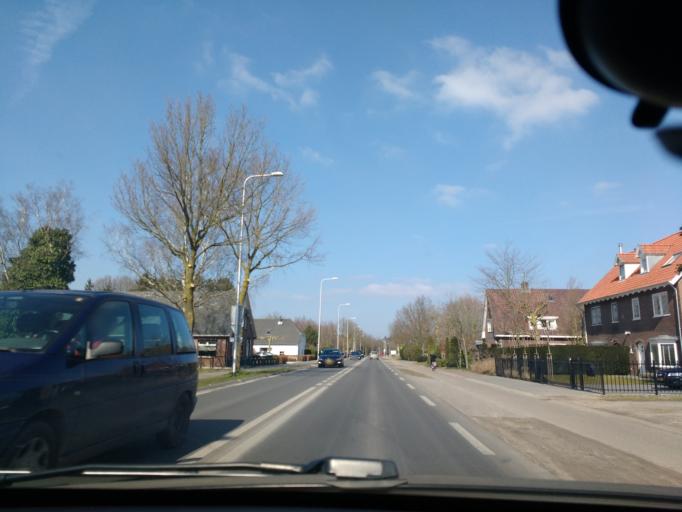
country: NL
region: Gelderland
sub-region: Gemeente Nijmegen
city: Nijmegen
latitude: 51.7922
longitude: 5.8497
